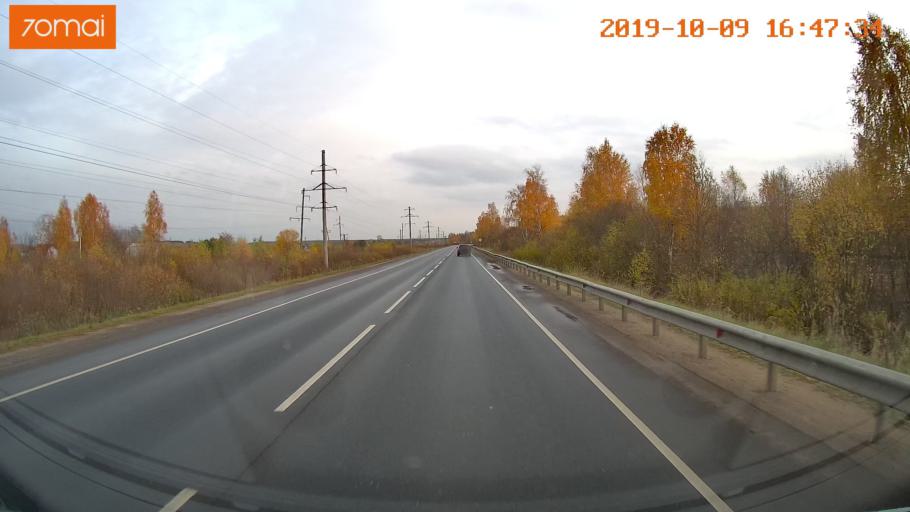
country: RU
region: Kostroma
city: Volgorechensk
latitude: 57.4361
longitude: 41.1792
